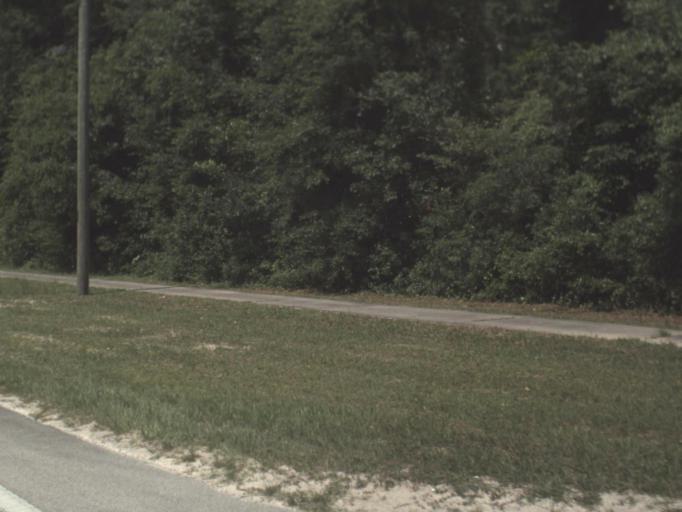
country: US
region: Florida
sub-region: Bradford County
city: Starke
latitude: 29.9608
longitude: -82.0163
